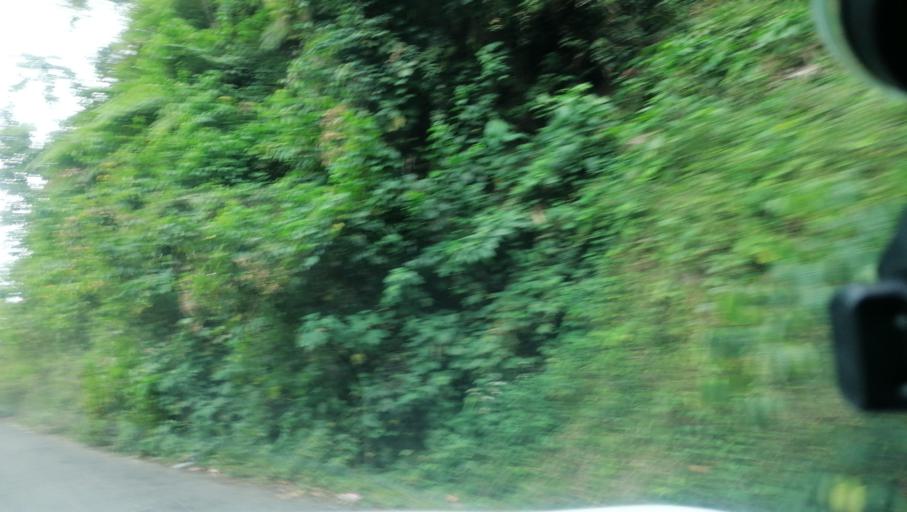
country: MX
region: Chiapas
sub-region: Cacahoatan
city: Benito Juarez
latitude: 15.0724
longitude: -92.1744
